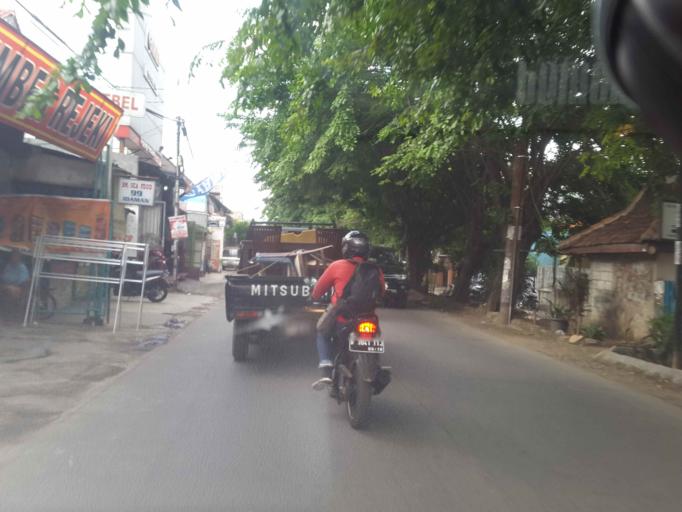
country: ID
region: West Java
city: Bekasi
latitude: -6.2898
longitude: 106.9164
